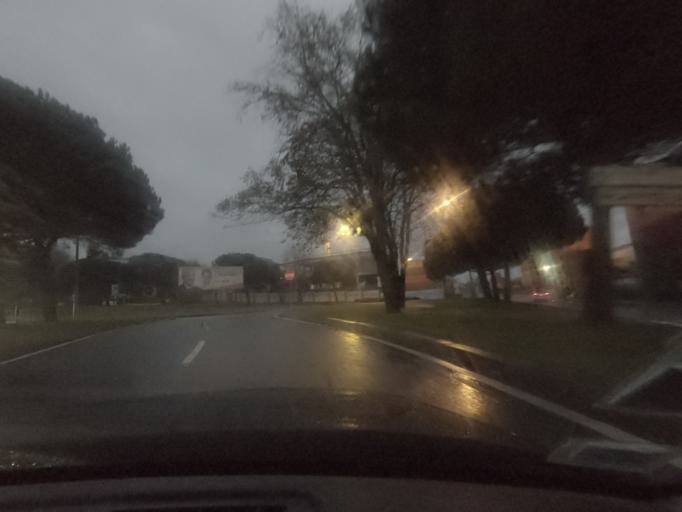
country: PT
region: Porto
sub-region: Matosinhos
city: Matosinhos
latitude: 41.1907
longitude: -8.6822
